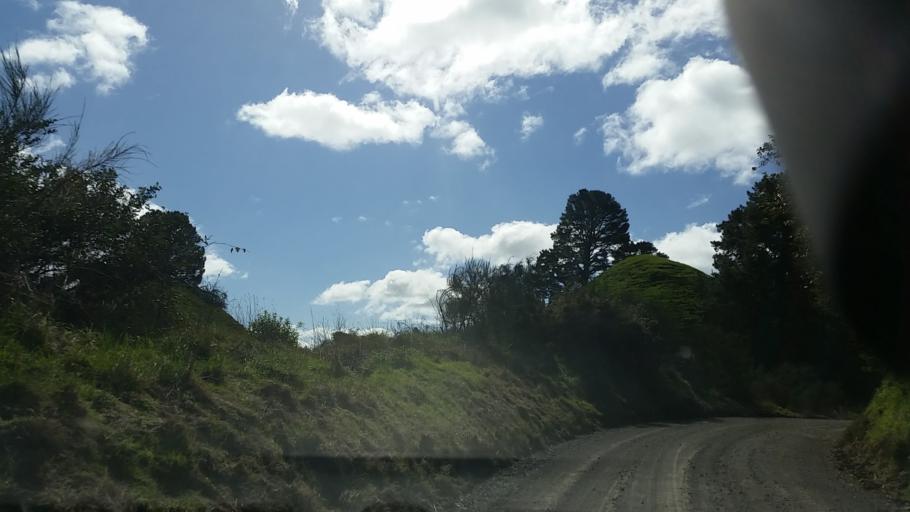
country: NZ
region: Waikato
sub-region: Taupo District
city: Taupo
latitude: -38.4790
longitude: 176.2168
